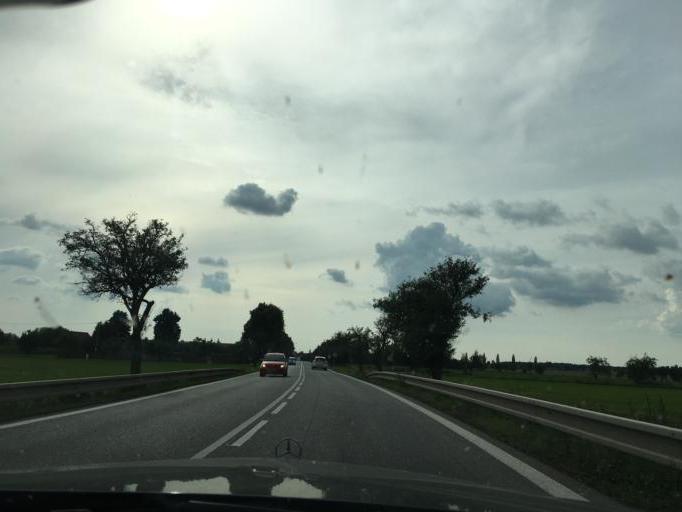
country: CZ
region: Kralovehradecky
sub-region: Okres Nachod
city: Jaromer
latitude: 50.3840
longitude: 15.9644
